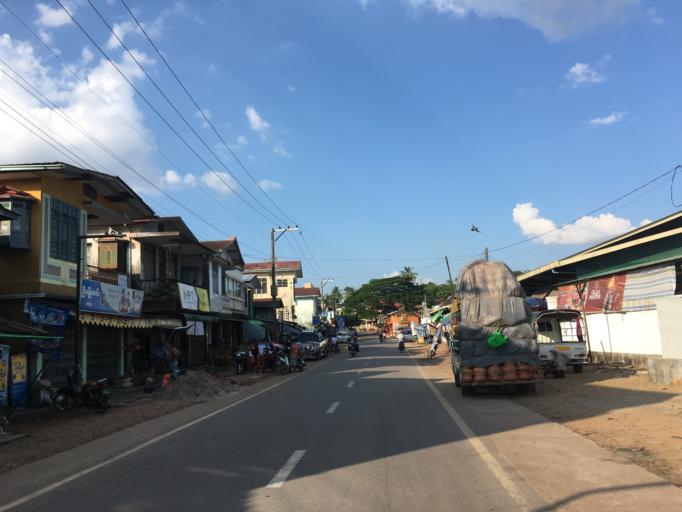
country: MM
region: Mon
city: Mawlamyine
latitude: 16.4555
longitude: 97.6261
